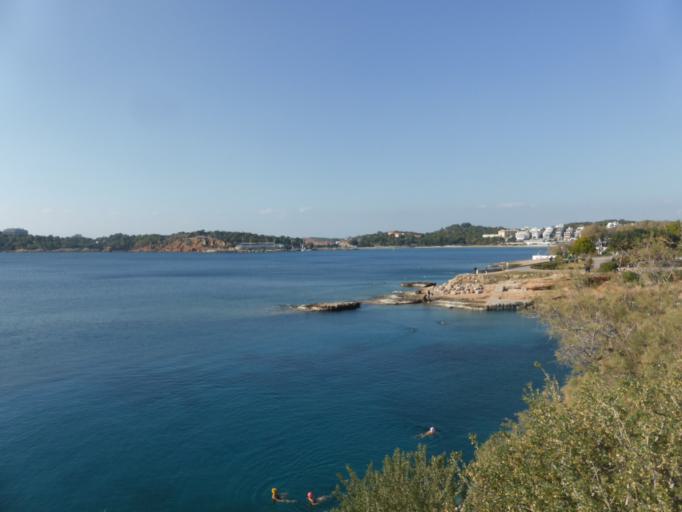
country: GR
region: Attica
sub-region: Nomarchia Anatolikis Attikis
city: Vouliagmeni
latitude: 37.8074
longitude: 23.7842
